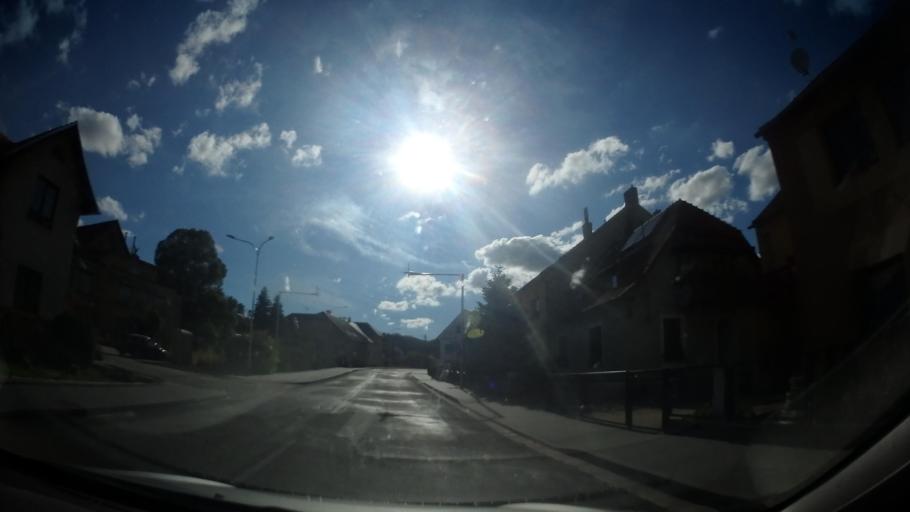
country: CZ
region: South Moravian
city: Lysice
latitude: 49.4506
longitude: 16.5414
